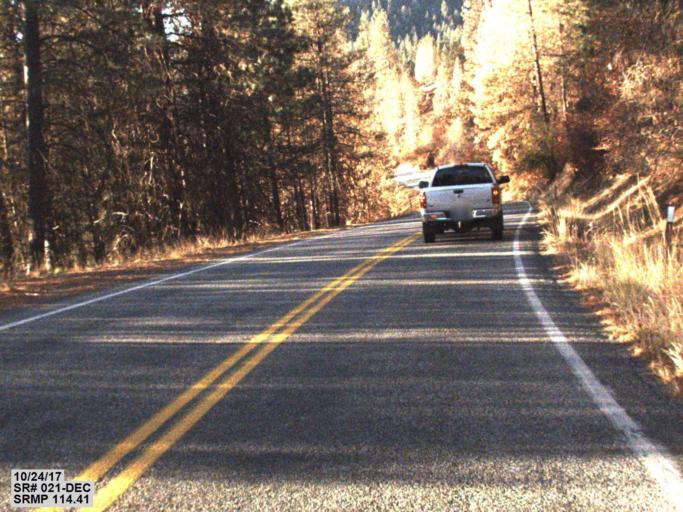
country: US
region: Washington
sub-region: Okanogan County
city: Coulee Dam
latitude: 48.0484
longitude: -118.6694
